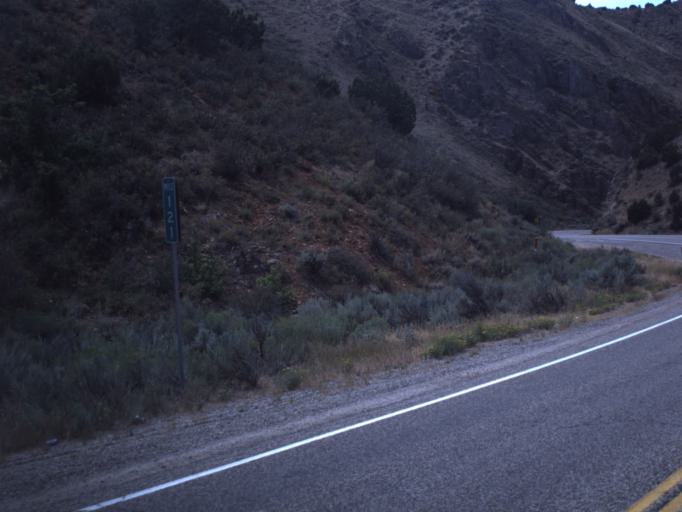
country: US
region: Utah
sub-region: Rich County
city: Randolph
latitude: 41.8245
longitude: -111.3016
